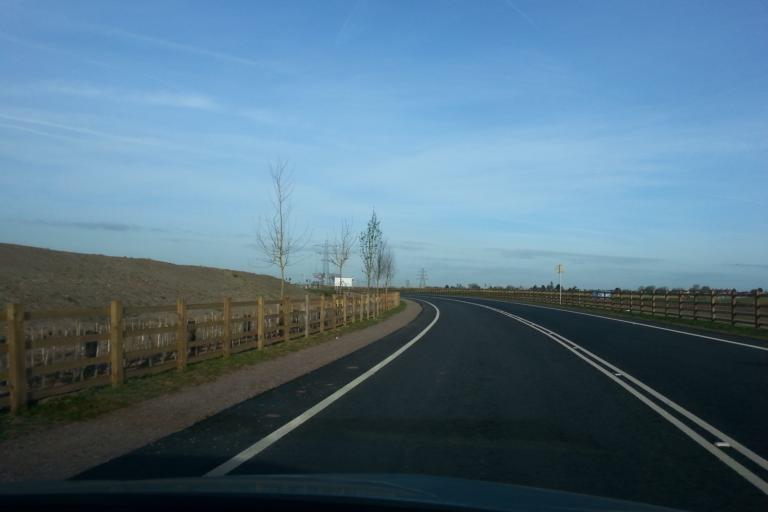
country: GB
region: England
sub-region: Nottinghamshire
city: Newark on Trent
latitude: 53.0519
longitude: -0.8025
